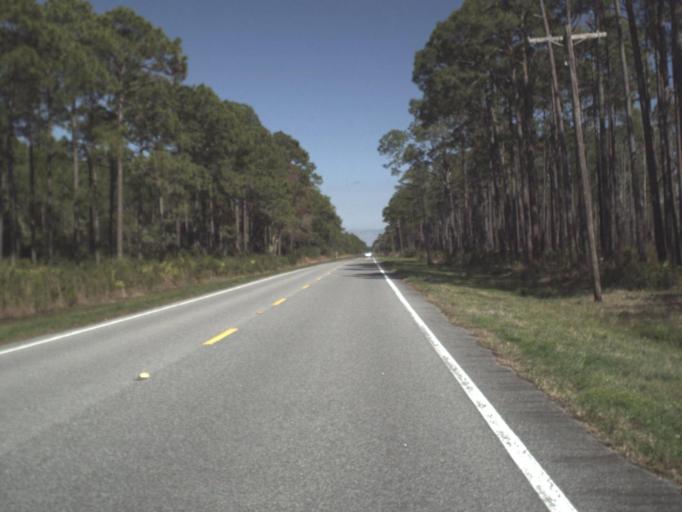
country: US
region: Florida
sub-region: Franklin County
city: Carrabelle
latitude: 29.9204
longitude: -84.4984
